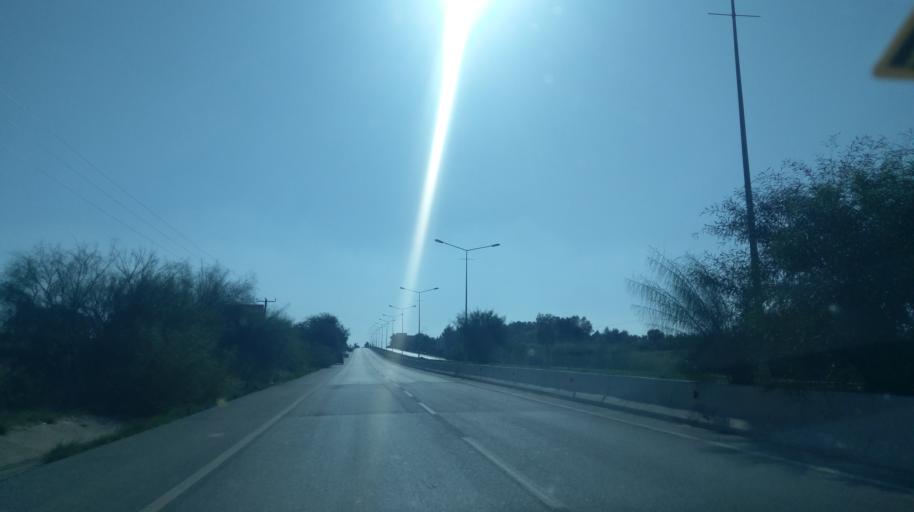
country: CY
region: Lefkosia
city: Geri
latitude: 35.1655
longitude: 33.5042
